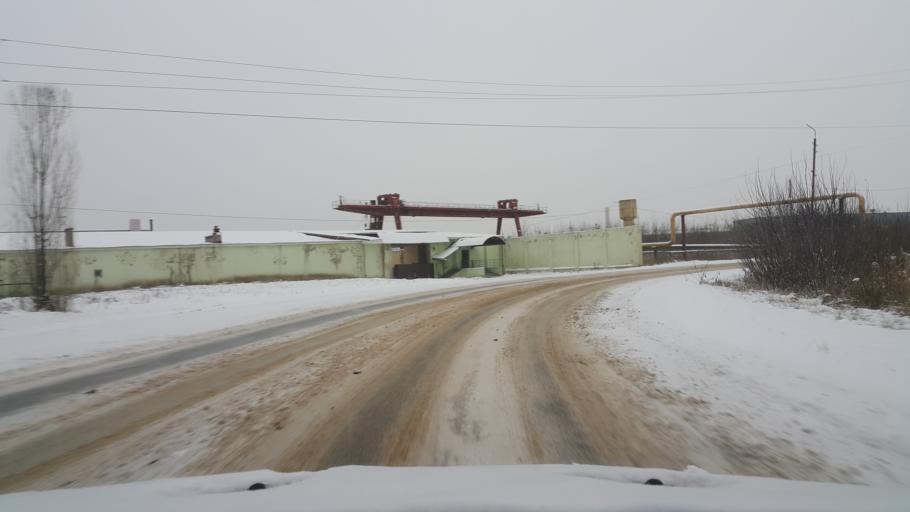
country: RU
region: Tambov
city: Pokrovo-Prigorodnoye
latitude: 52.6590
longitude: 41.4231
